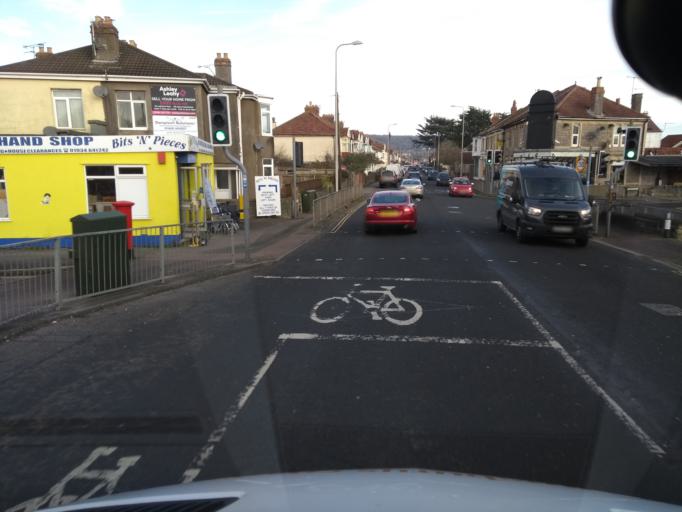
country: GB
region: England
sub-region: North Somerset
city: Weston-super-Mare
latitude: 51.3374
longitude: -2.9703
